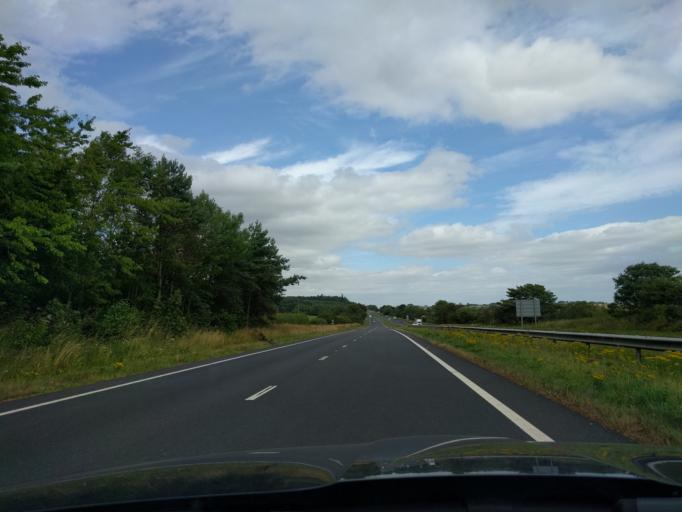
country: GB
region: England
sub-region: Northumberland
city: Felton
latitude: 55.3219
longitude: -1.7247
